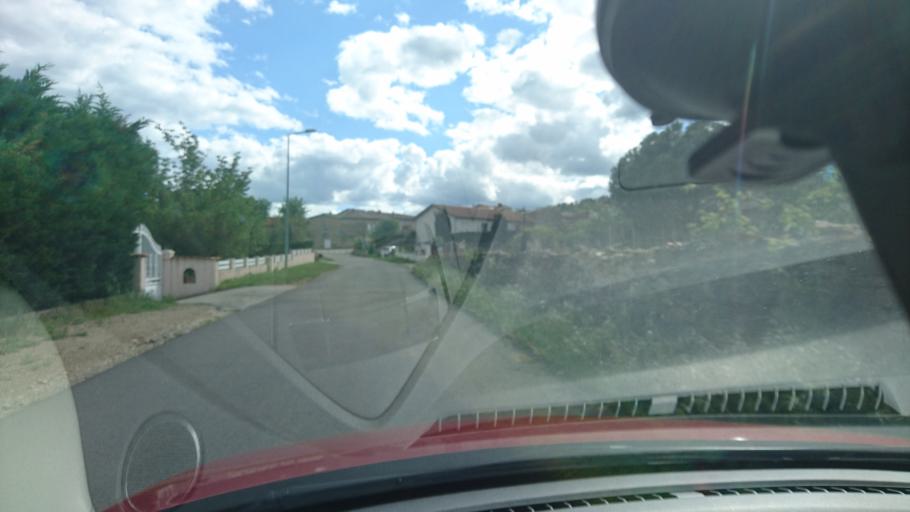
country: FR
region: Rhone-Alpes
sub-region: Departement de la Loire
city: Saint-Pierre-de-Boeuf
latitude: 45.3677
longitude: 4.7337
